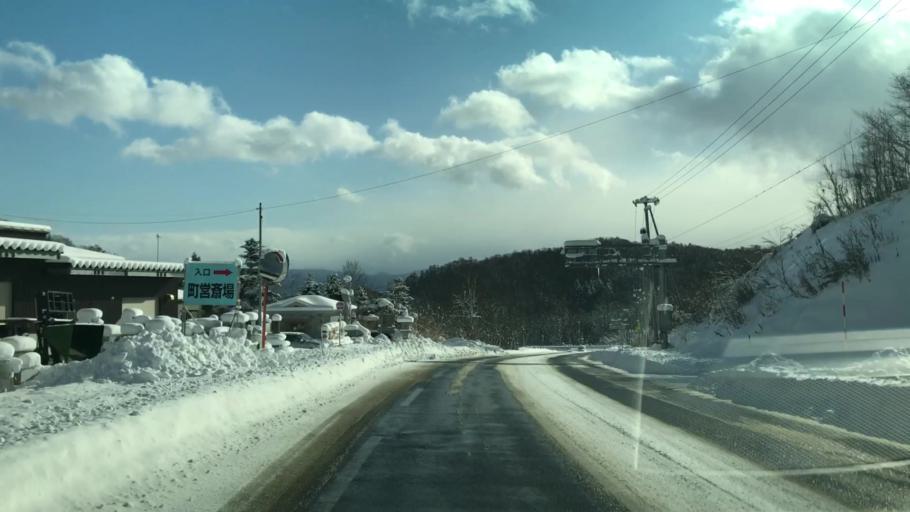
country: JP
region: Hokkaido
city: Yoichi
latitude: 43.2191
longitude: 140.7415
